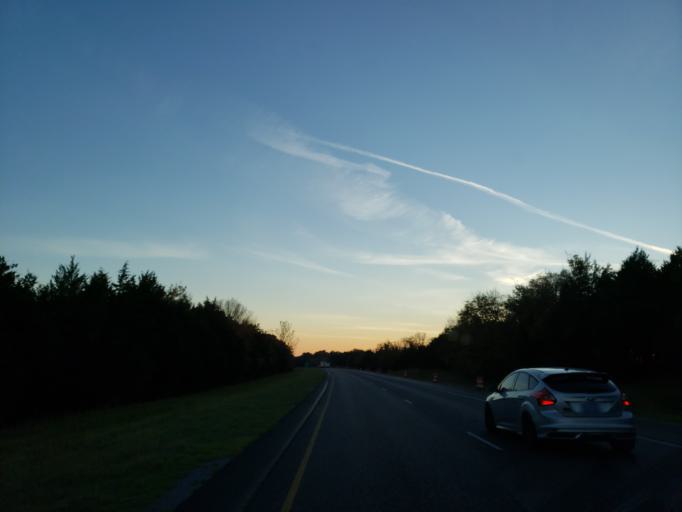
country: US
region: Alabama
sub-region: Sumter County
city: Livingston
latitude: 32.6480
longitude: -88.1946
